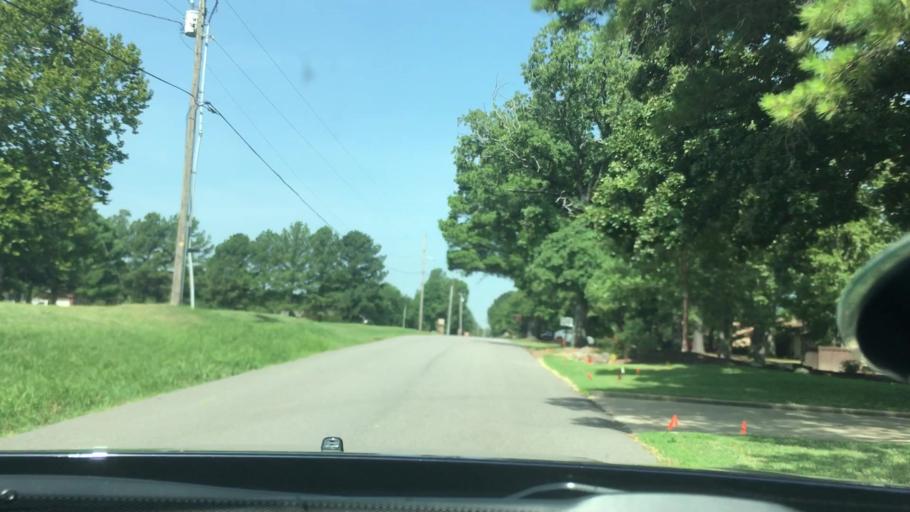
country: US
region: Oklahoma
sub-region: Atoka County
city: Atoka
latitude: 34.3603
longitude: -96.1467
